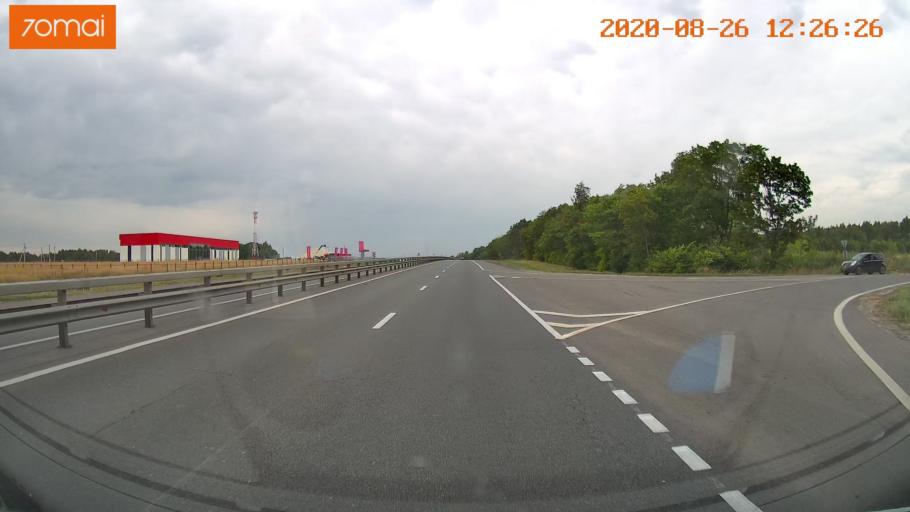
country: RU
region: Rjazan
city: Polyany
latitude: 54.5351
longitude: 39.8601
